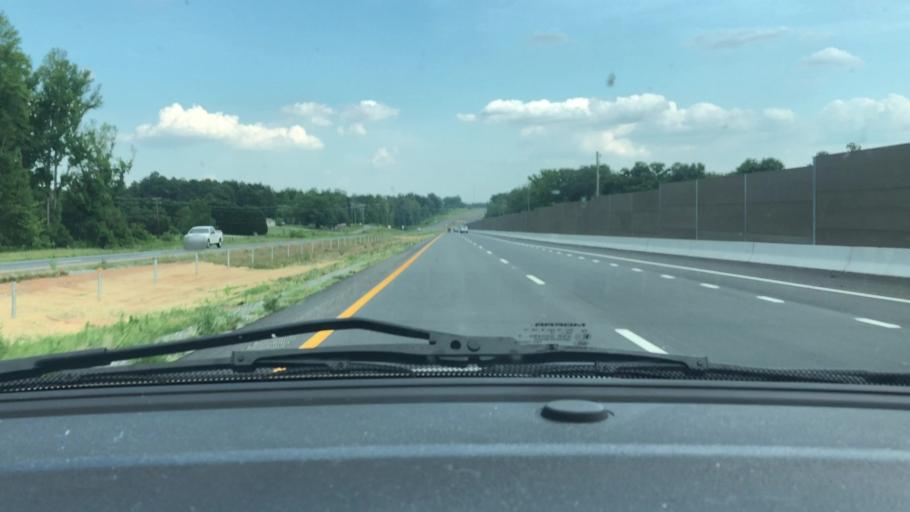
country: US
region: North Carolina
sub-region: Guilford County
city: Stokesdale
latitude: 36.2628
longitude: -79.9280
